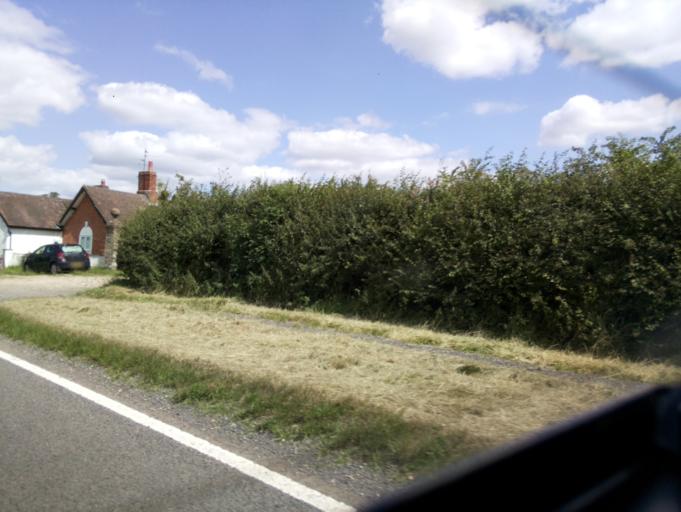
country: GB
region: England
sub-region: Buckinghamshire
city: Aylesbury
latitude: 51.8562
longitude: -0.8293
